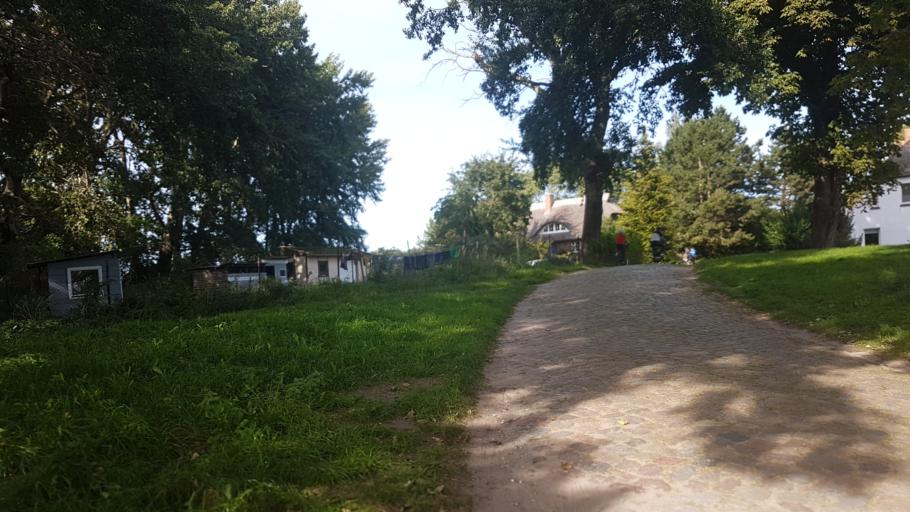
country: DE
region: Mecklenburg-Vorpommern
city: Gingst
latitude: 54.4309
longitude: 13.2059
